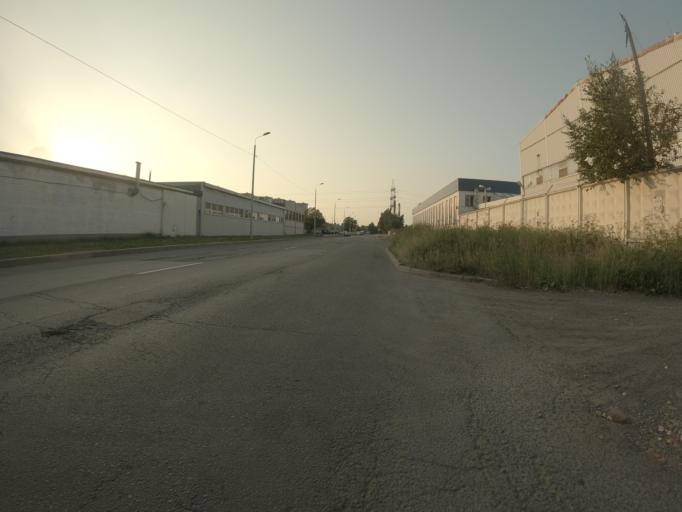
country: RU
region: St.-Petersburg
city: Krasnogvargeisky
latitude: 59.9727
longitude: 30.4408
